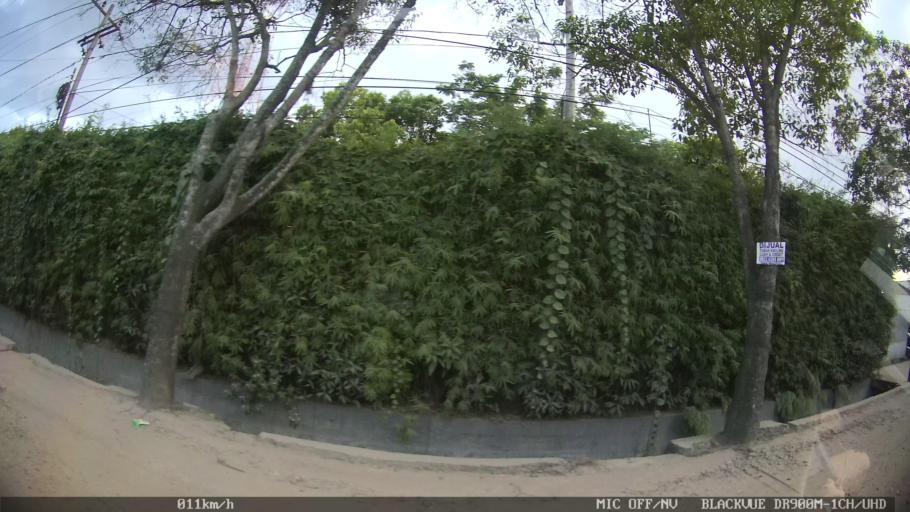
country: ID
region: North Sumatra
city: Medan
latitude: 3.5969
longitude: 98.7384
